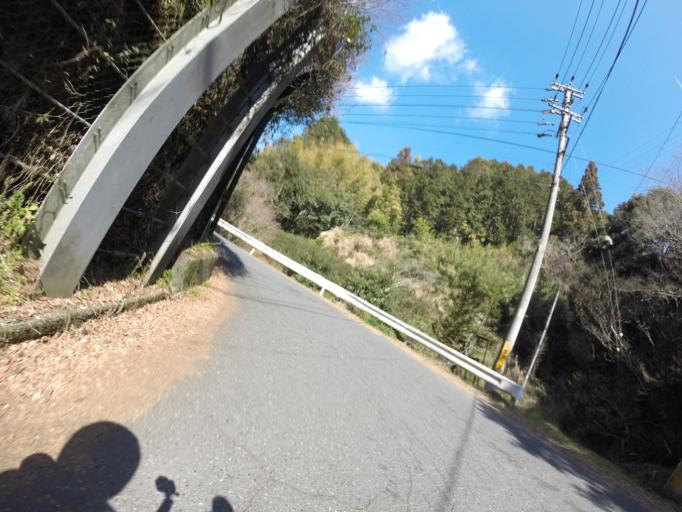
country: JP
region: Shizuoka
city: Shizuoka-shi
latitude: 35.0803
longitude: 138.4757
